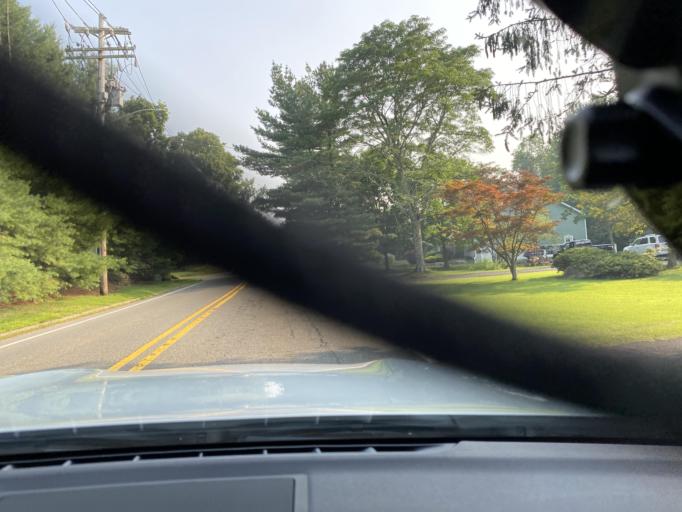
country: US
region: New York
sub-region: Rockland County
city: Airmont
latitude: 41.0880
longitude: -74.1263
